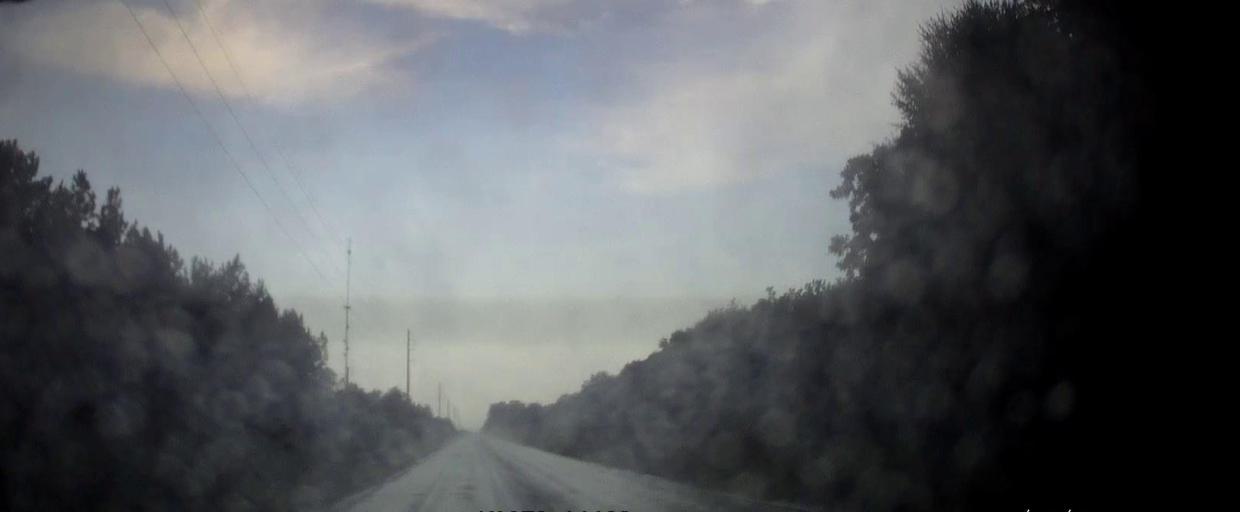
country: US
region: Georgia
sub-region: Dodge County
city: Chester
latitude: 32.5689
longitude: -83.1834
